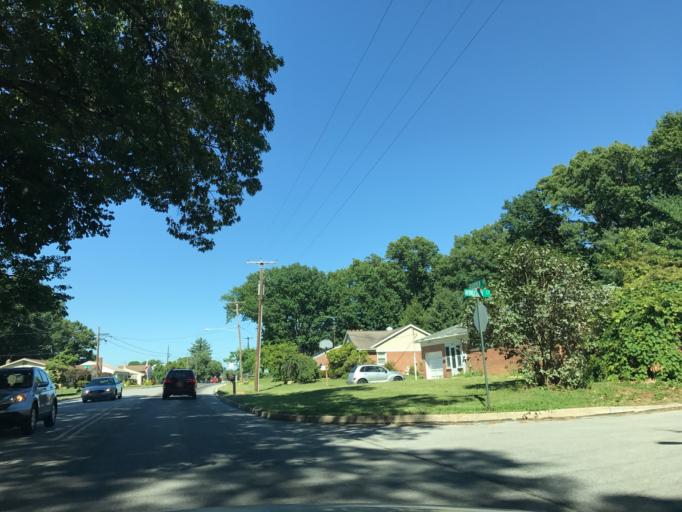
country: US
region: Pennsylvania
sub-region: York County
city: Parkville
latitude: 39.7716
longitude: -76.9671
